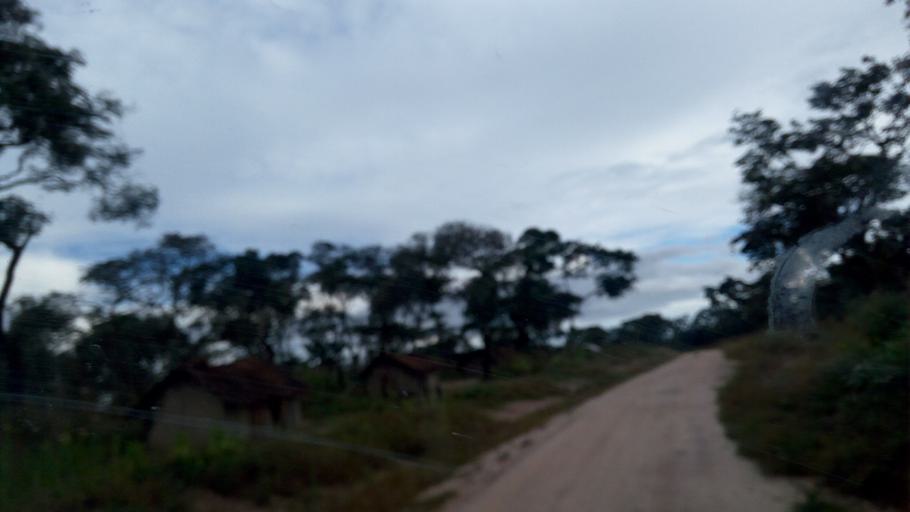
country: CD
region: Katanga
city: Kalemie
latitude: -6.5996
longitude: 29.0415
